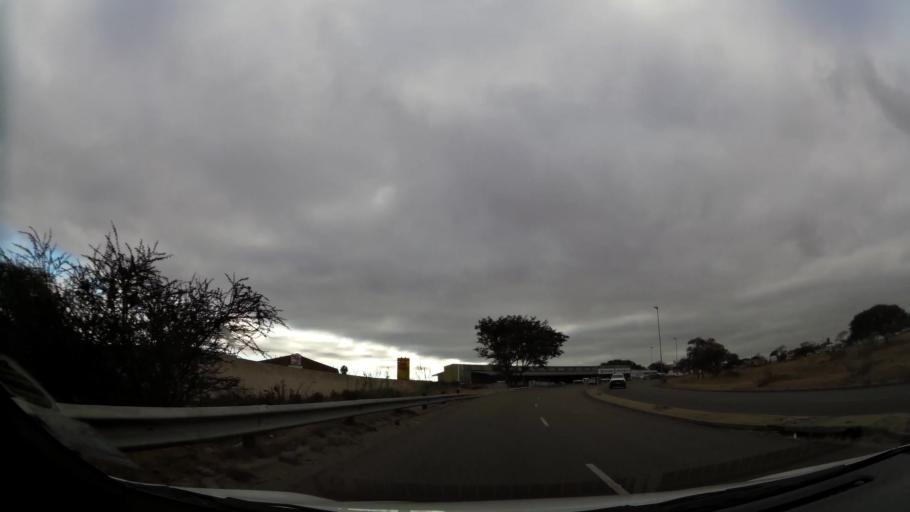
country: ZA
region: Limpopo
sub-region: Capricorn District Municipality
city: Polokwane
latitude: -23.8781
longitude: 29.4341
